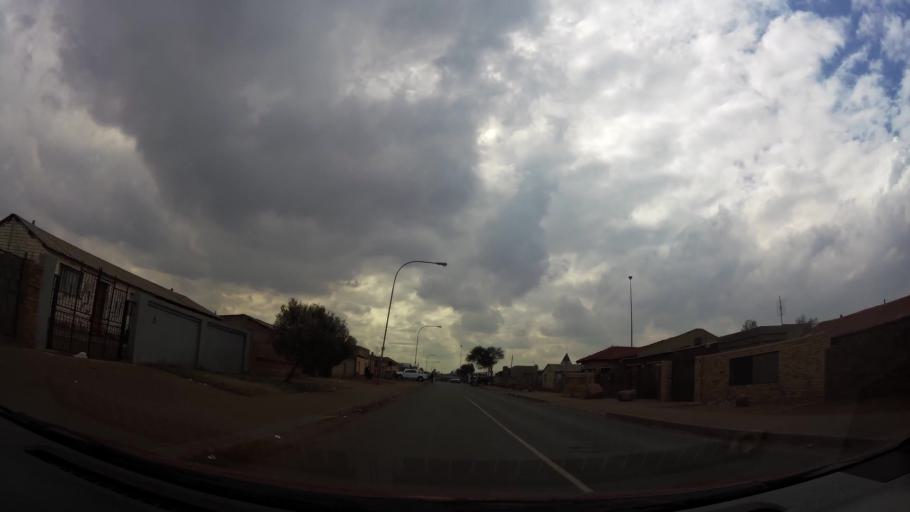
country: ZA
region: Gauteng
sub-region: City of Johannesburg Metropolitan Municipality
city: Soweto
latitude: -26.2551
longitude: 27.8298
